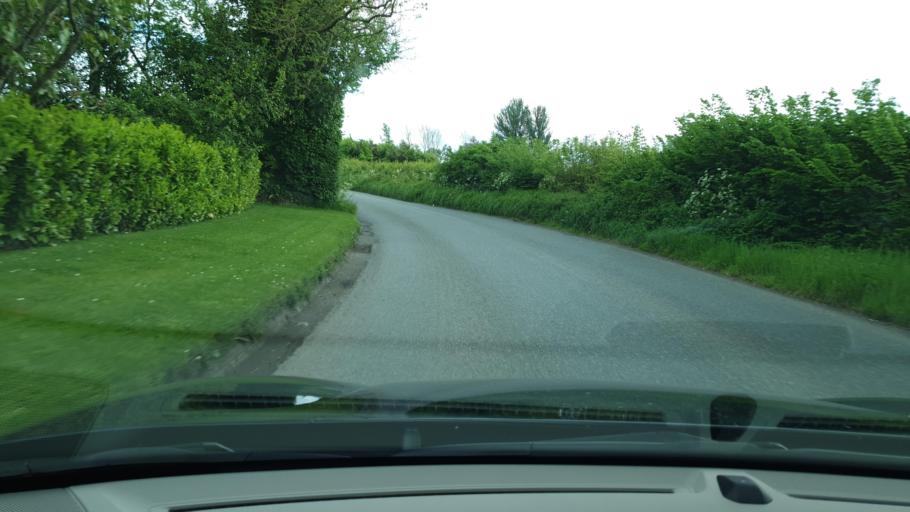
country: IE
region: Leinster
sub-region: An Mhi
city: Ashbourne
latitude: 53.5324
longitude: -6.4273
